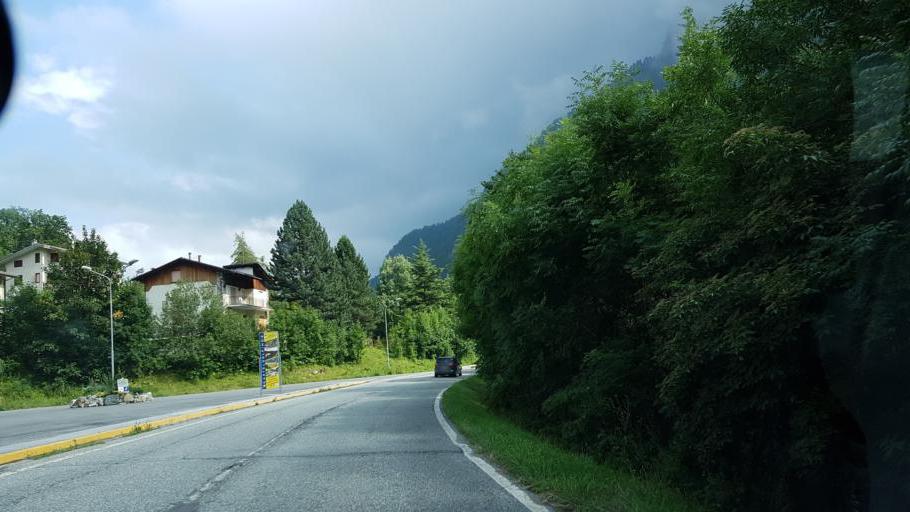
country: IT
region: Piedmont
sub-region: Provincia di Cuneo
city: Casteldelfino
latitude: 44.5876
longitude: 7.0758
